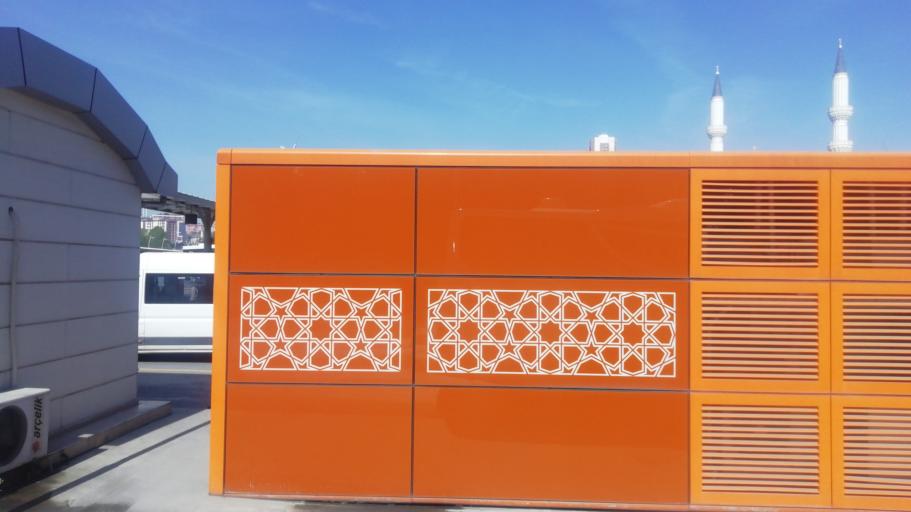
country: TR
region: Istanbul
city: Sisli
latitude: 41.0876
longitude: 28.9468
